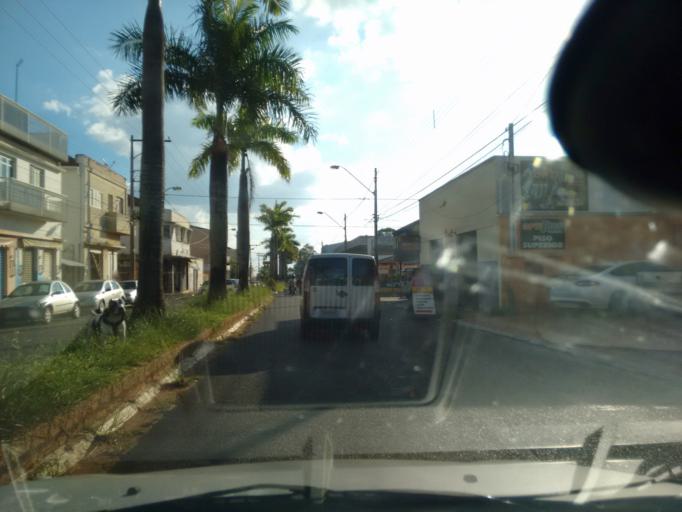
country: BR
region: Sao Paulo
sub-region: Araraquara
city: Araraquara
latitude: -21.8009
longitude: -48.1865
